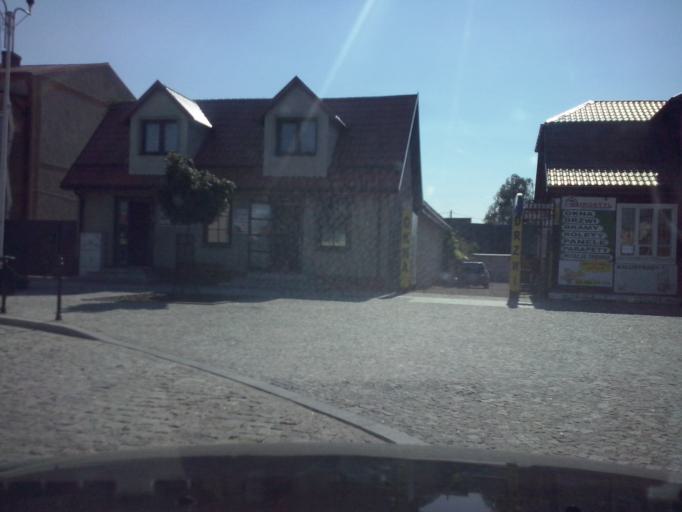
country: PL
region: Swietokrzyskie
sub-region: Powiat kielecki
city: Daleszyce
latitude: 50.8019
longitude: 20.8055
